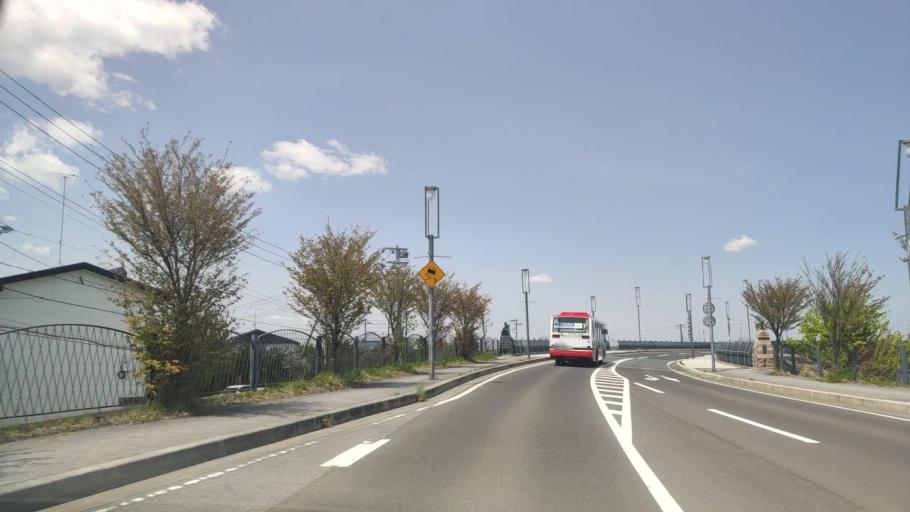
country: JP
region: Aomori
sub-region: Hachinohe Shi
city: Uchimaru
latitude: 40.4995
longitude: 141.4447
